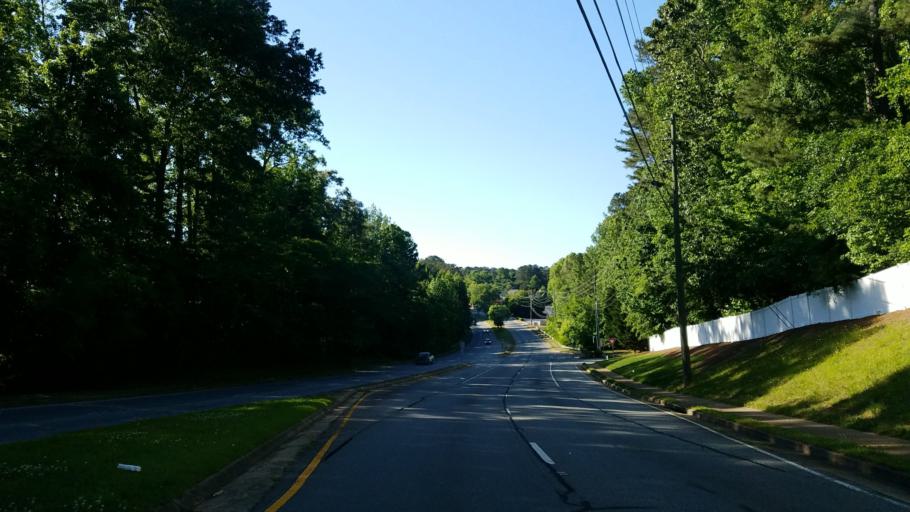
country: US
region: Georgia
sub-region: Cherokee County
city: Woodstock
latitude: 34.0728
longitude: -84.5705
